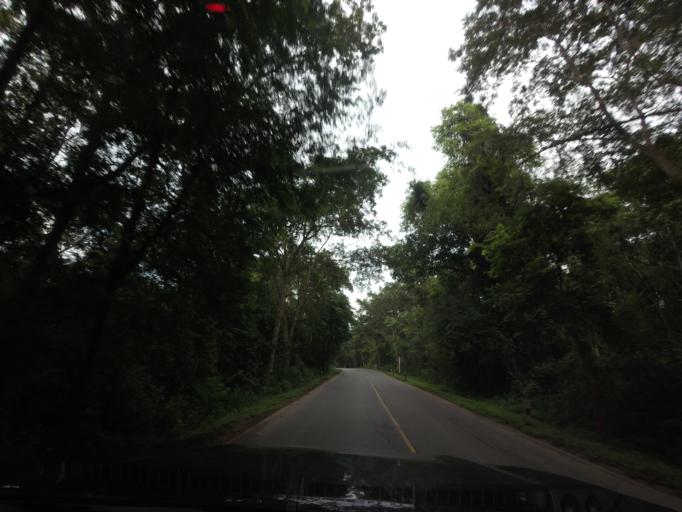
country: TH
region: Changwat Nong Bua Lamphu
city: Suwannakhuha
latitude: 17.4946
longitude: 102.3702
